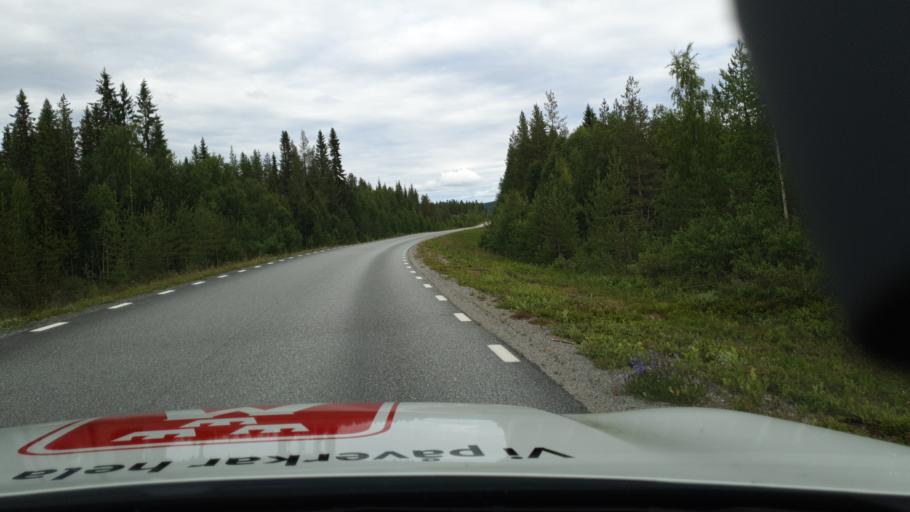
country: SE
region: Vaesterbotten
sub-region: Sorsele Kommun
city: Sorsele
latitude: 65.5265
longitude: 17.3903
